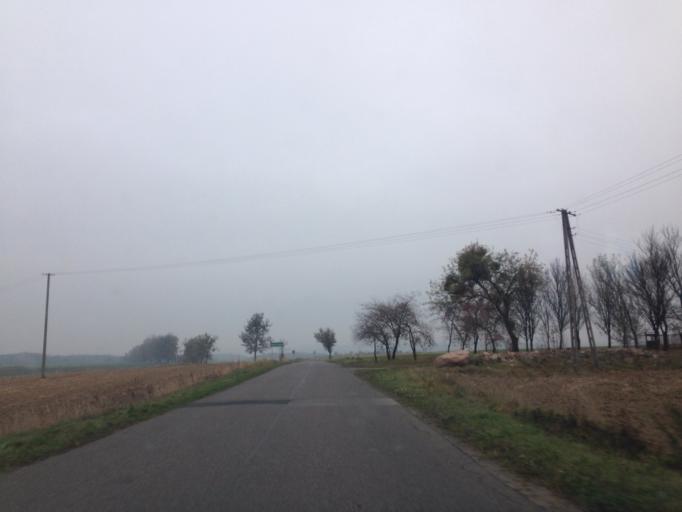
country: PL
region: Kujawsko-Pomorskie
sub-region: Powiat brodnicki
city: Bartniczka
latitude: 53.2354
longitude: 19.6005
